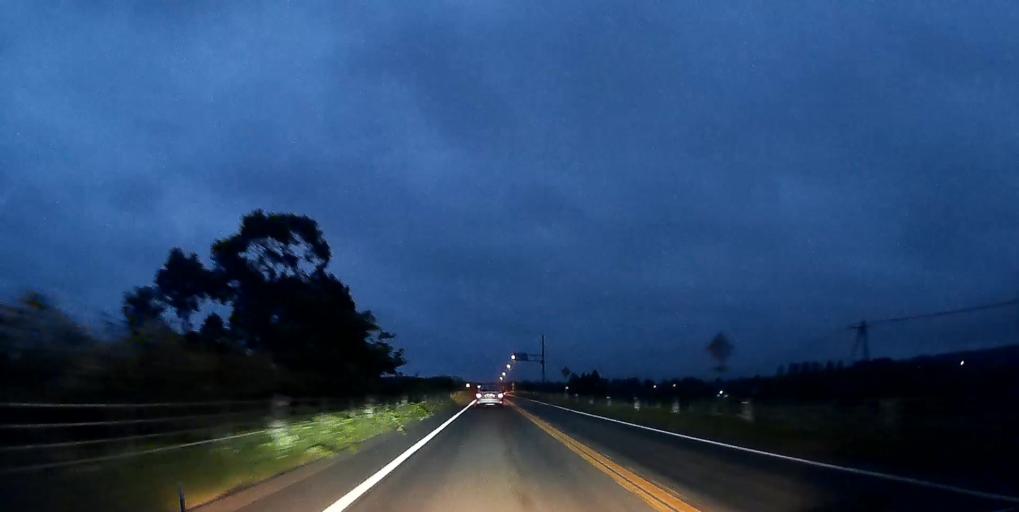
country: JP
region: Hokkaido
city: Nanae
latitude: 42.2112
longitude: 140.3932
